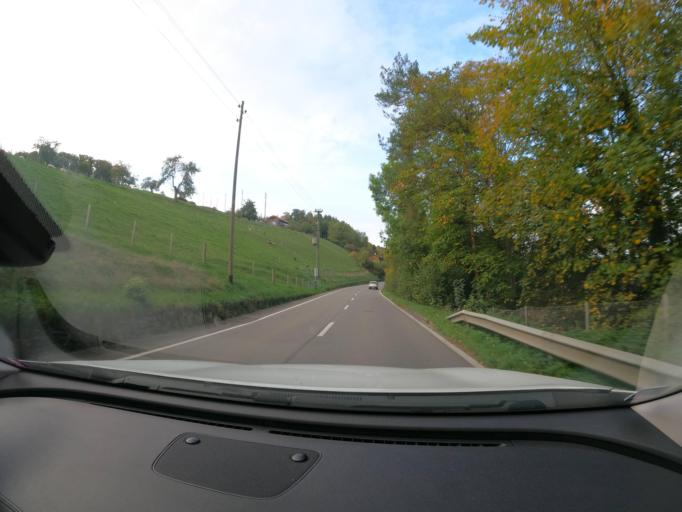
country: CH
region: Bern
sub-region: Bern-Mittelland District
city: Toffen
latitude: 46.8724
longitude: 7.4924
